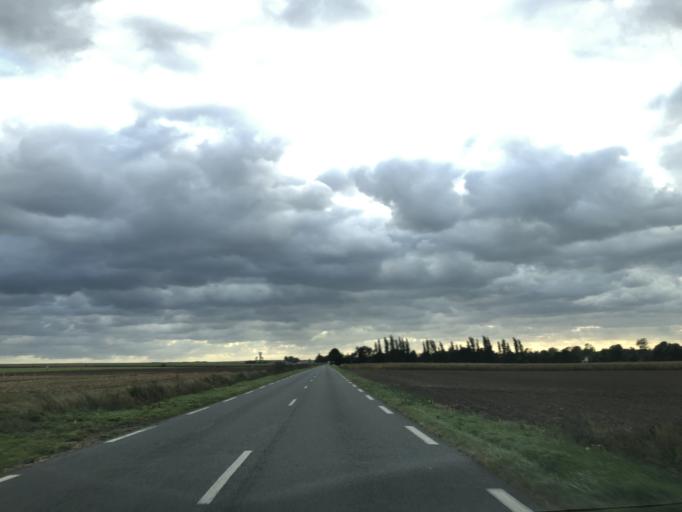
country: FR
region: Picardie
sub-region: Departement de la Somme
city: Pende
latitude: 50.1487
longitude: 1.5421
